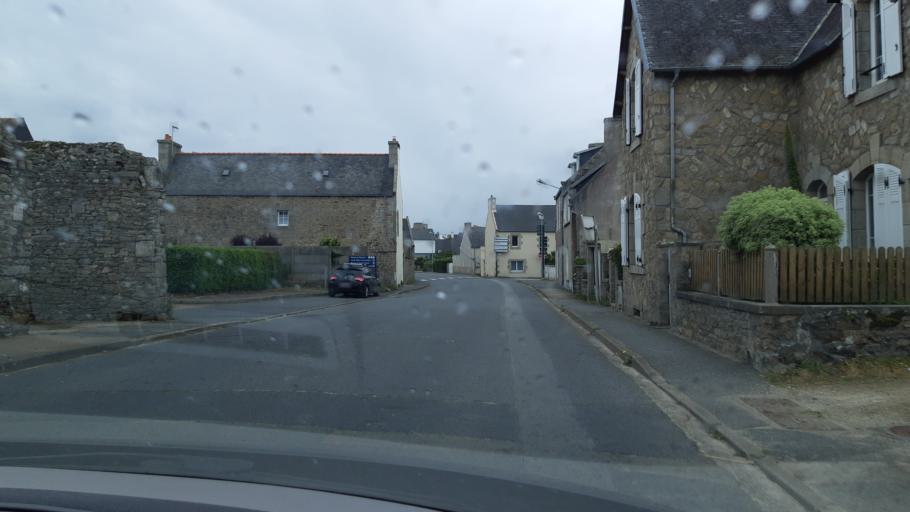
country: FR
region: Brittany
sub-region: Departement du Finistere
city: Roscoff
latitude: 48.7182
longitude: -3.9851
